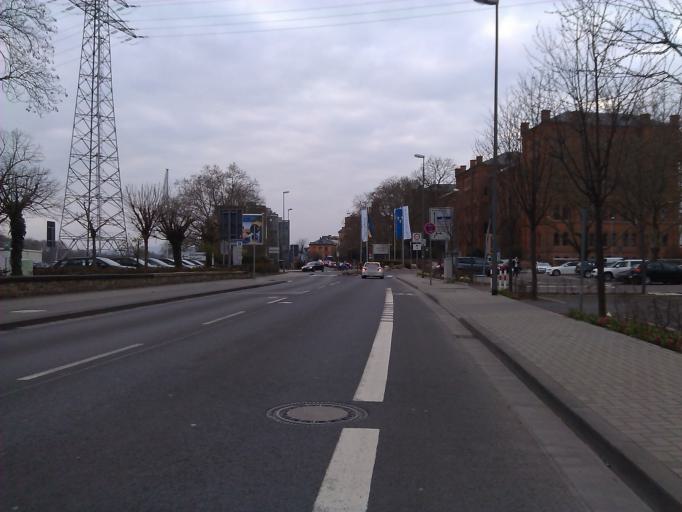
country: DE
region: Hesse
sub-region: Regierungsbezirk Darmstadt
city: Wiesbaden
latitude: 50.0340
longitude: 8.2447
